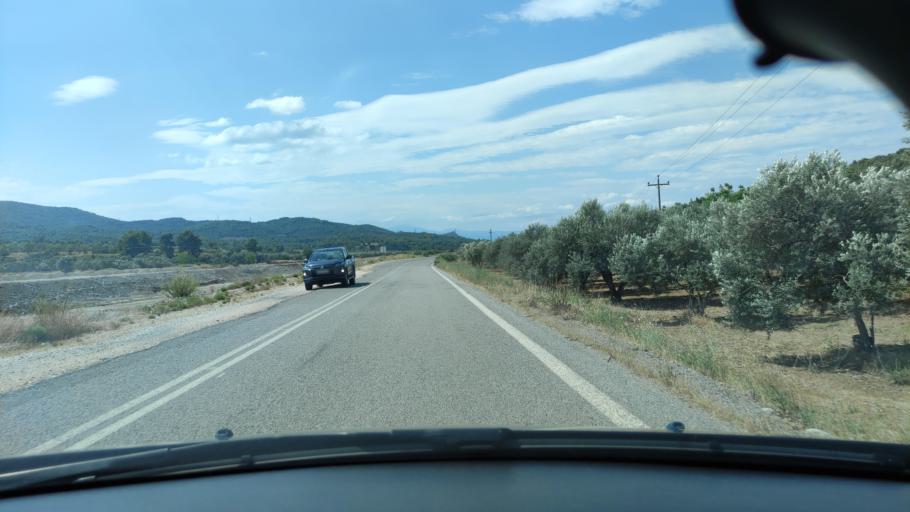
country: GR
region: Central Greece
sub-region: Nomos Evvoias
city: Afration
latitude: 38.4882
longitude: 23.6892
